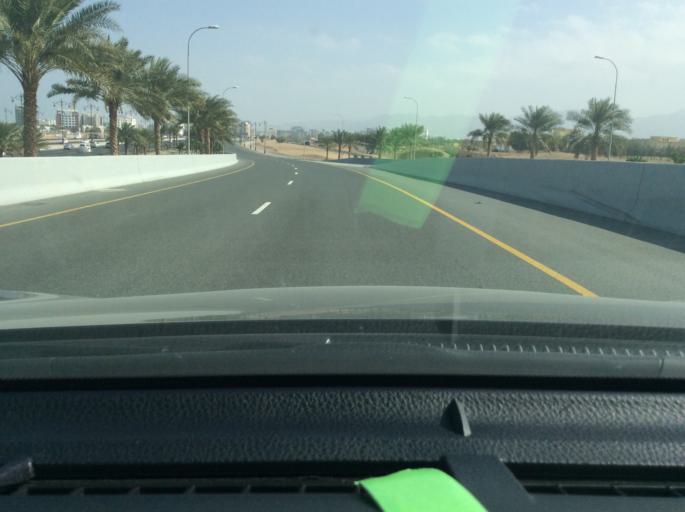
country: OM
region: Muhafazat Masqat
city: Bawshar
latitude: 23.5923
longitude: 58.3397
